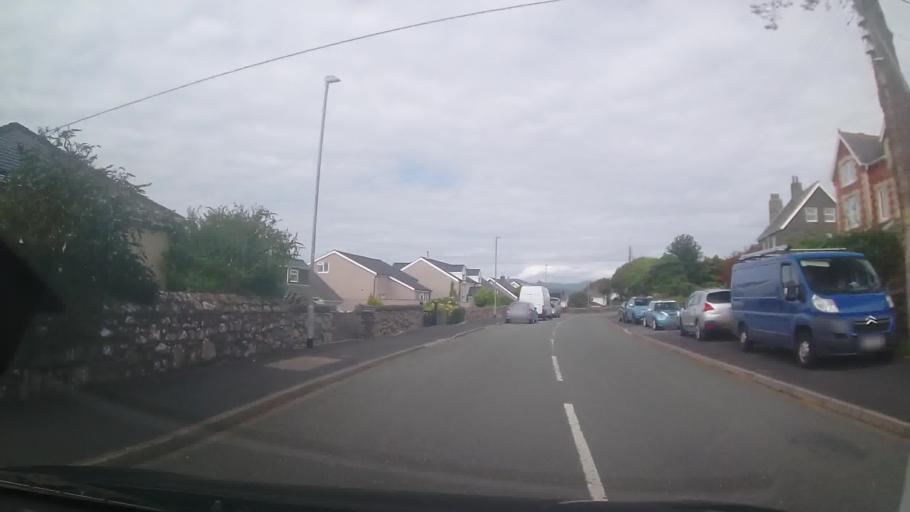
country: GB
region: Wales
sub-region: Gwynedd
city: Barmouth
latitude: 52.6710
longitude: -4.0828
